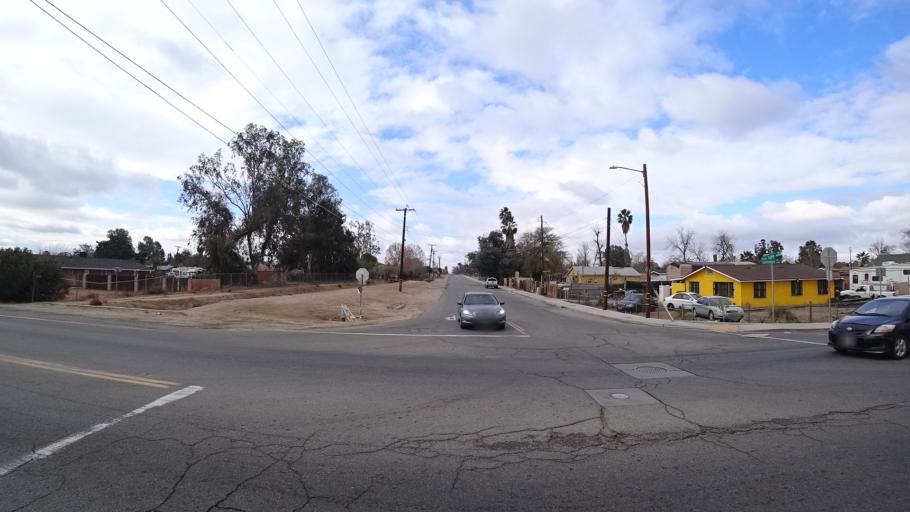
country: US
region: California
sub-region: Kern County
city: Bakersfield
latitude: 35.3394
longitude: -118.9855
